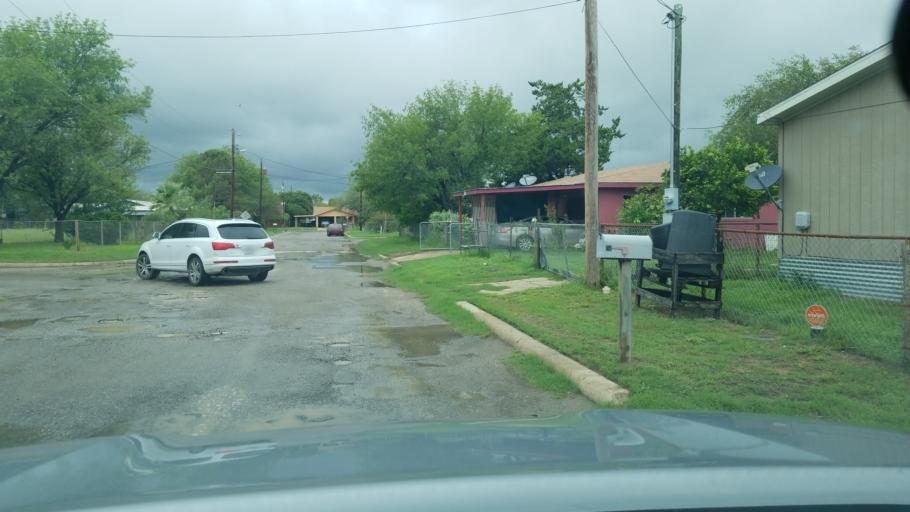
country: US
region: Texas
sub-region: Dimmit County
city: Carrizo Springs
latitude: 28.5314
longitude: -99.8492
